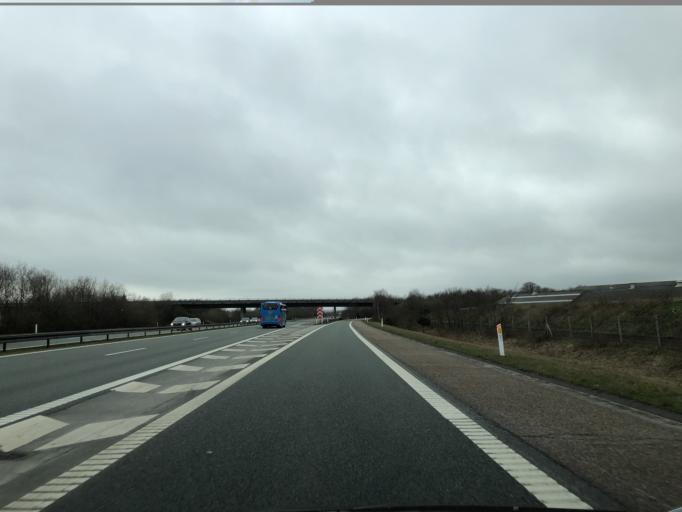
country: DK
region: North Denmark
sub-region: Bronderslev Kommune
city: Hjallerup
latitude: 57.1553
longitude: 10.1673
